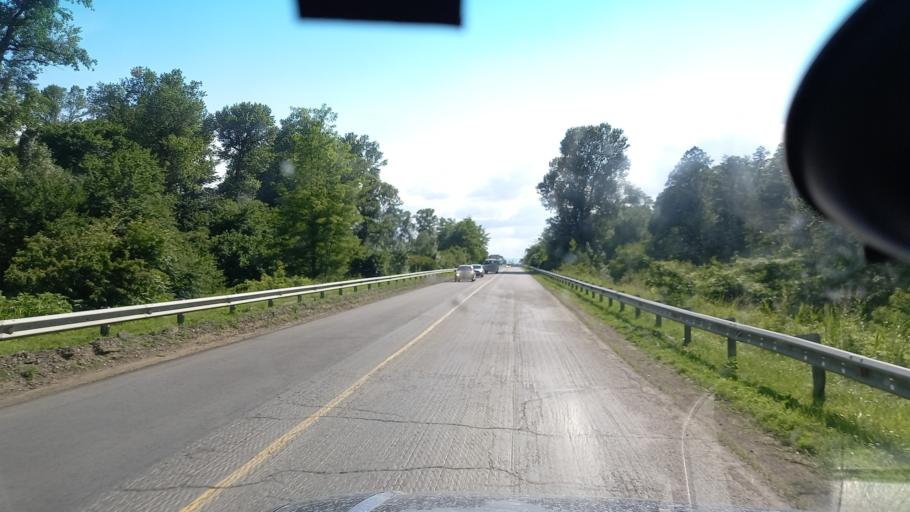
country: RU
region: Krasnodarskiy
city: Mostovskoy
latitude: 44.4023
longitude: 40.8270
